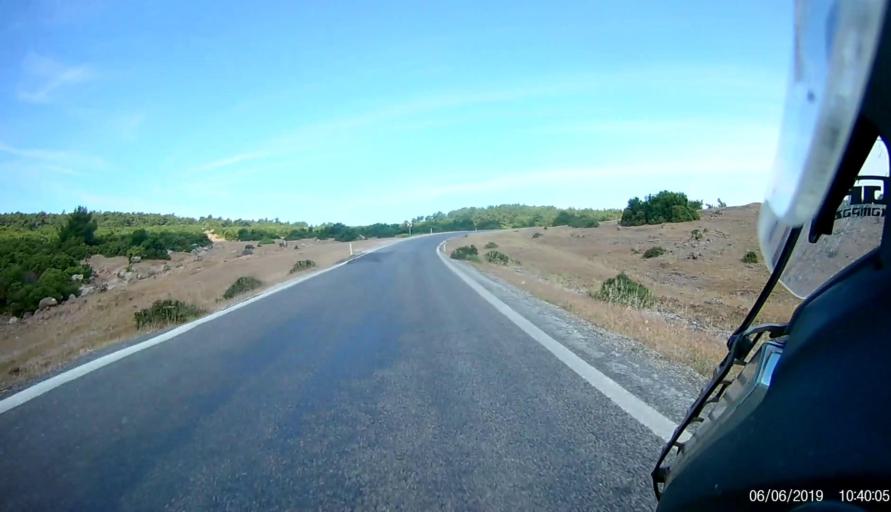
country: TR
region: Canakkale
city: Ayvacik
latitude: 39.5209
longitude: 26.4556
